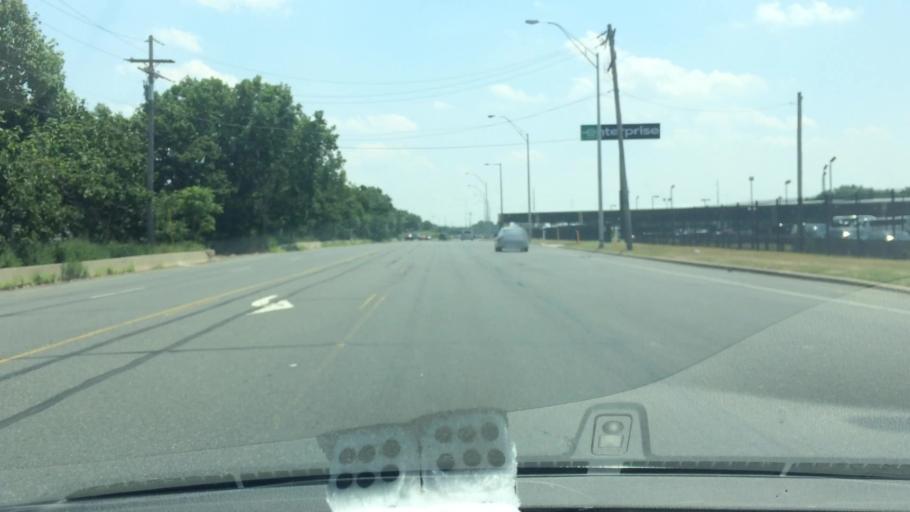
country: US
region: Pennsylvania
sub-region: Delaware County
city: Colwyn
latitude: 39.9012
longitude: -75.2251
